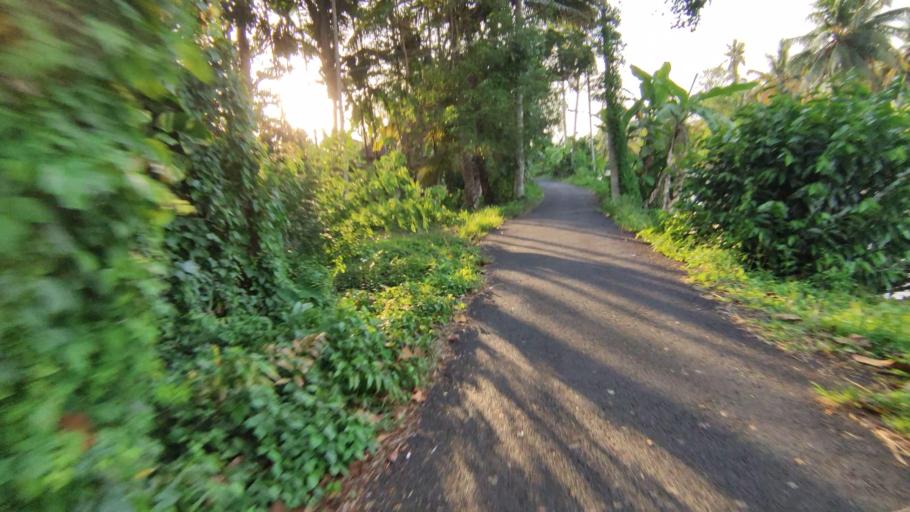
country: IN
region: Kerala
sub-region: Kottayam
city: Kottayam
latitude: 9.5771
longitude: 76.4438
